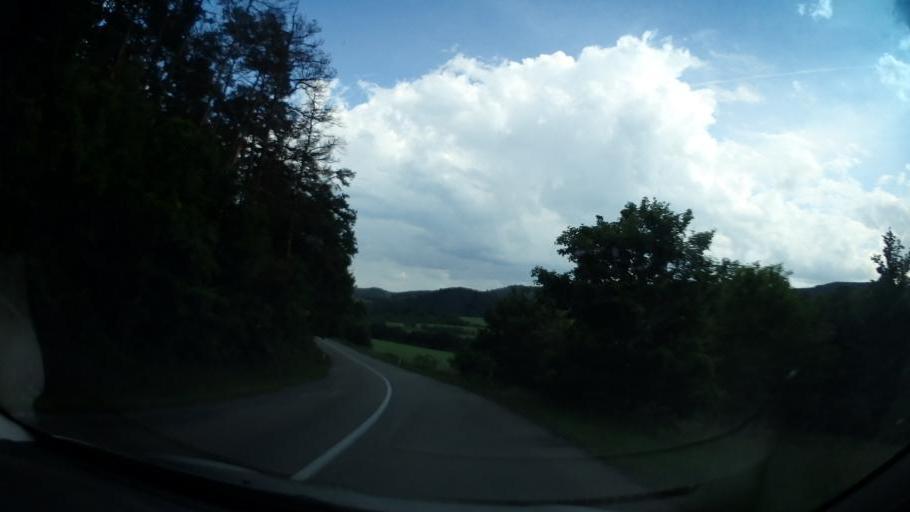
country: CZ
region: South Moravian
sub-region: Okres Brno-Venkov
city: Dolni Loucky
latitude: 49.3658
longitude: 16.3773
